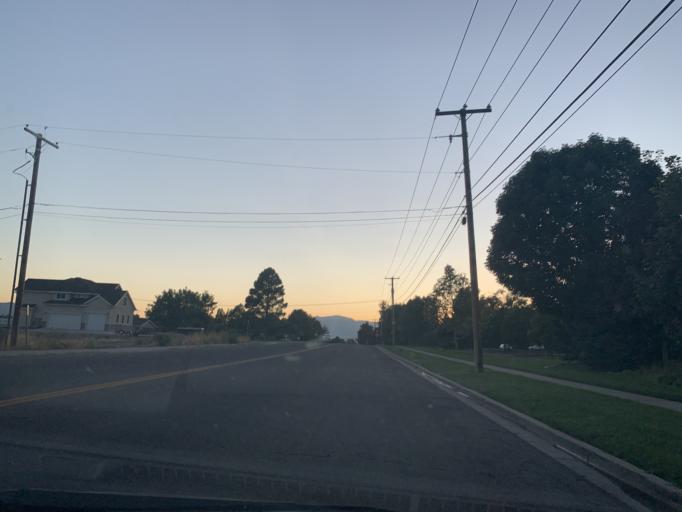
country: US
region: Utah
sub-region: Utah County
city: Cedar Hills
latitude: 40.3919
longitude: -111.7714
